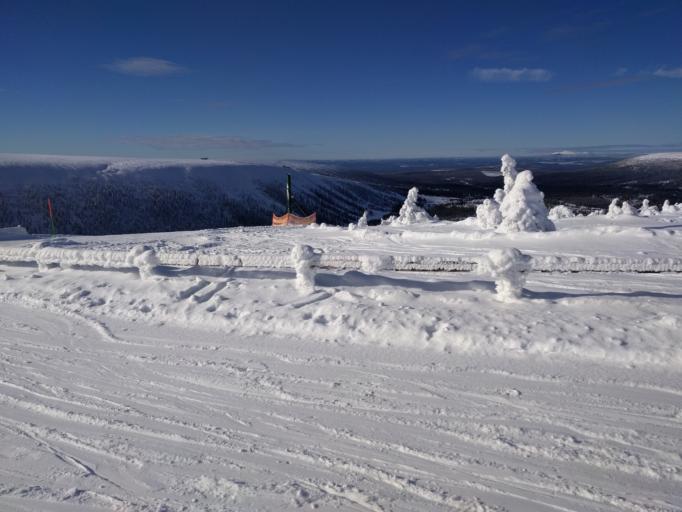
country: NO
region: Hedmark
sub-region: Trysil
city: Innbygda
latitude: 61.1731
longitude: 13.0161
